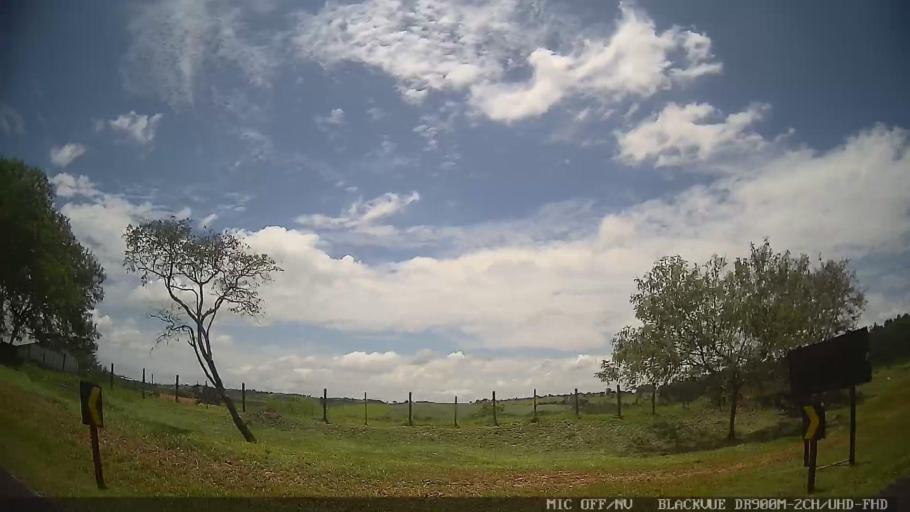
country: BR
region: Sao Paulo
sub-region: Laranjal Paulista
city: Laranjal Paulista
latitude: -23.0508
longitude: -47.8224
